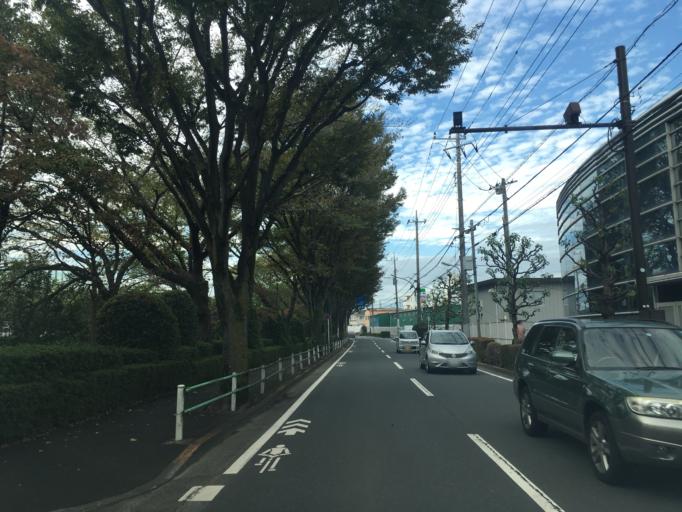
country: JP
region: Tokyo
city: Chofugaoka
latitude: 35.6396
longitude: 139.5499
